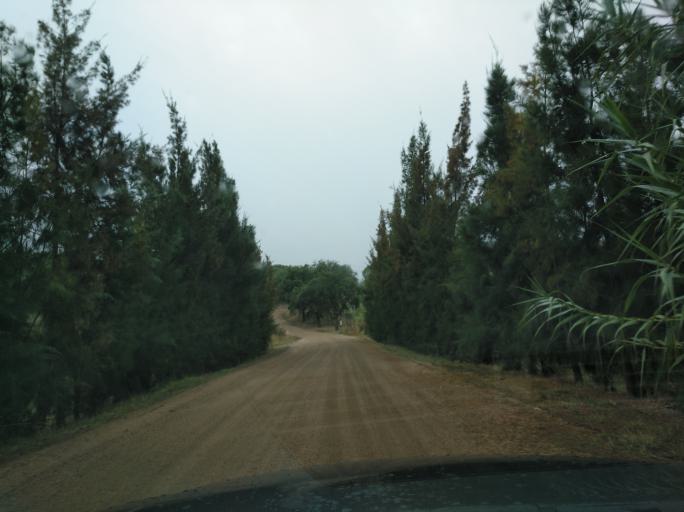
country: PT
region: Portalegre
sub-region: Campo Maior
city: Campo Maior
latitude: 38.9512
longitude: -7.0708
